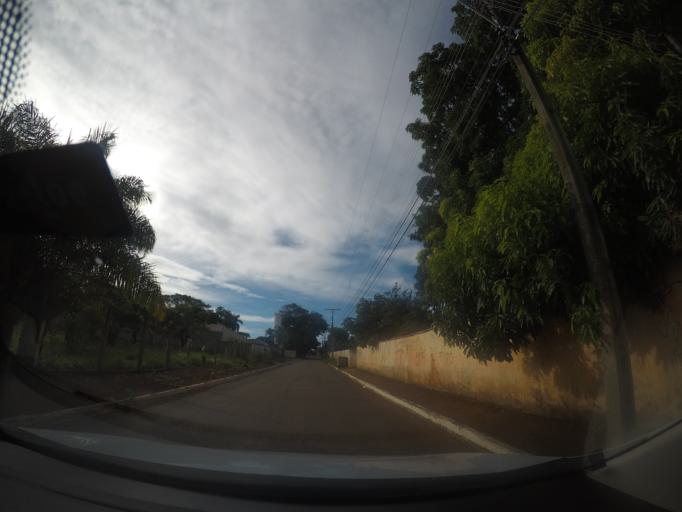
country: BR
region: Goias
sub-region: Goiania
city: Goiania
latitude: -16.6340
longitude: -49.3517
